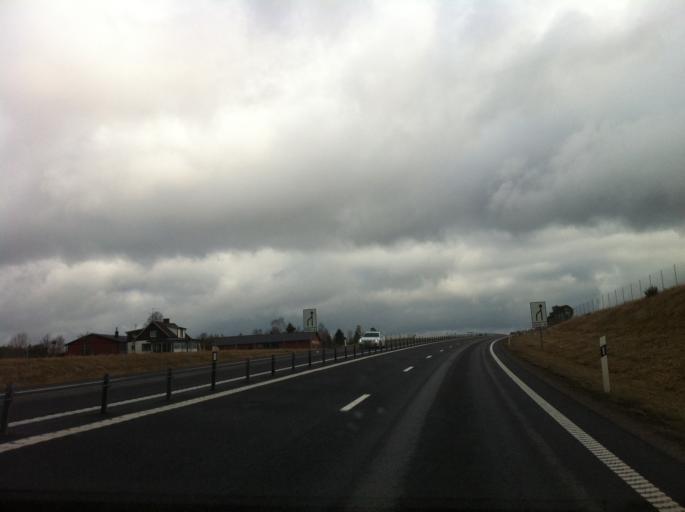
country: SE
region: Halland
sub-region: Halmstads Kommun
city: Oskarstrom
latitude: 56.8651
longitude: 13.0364
